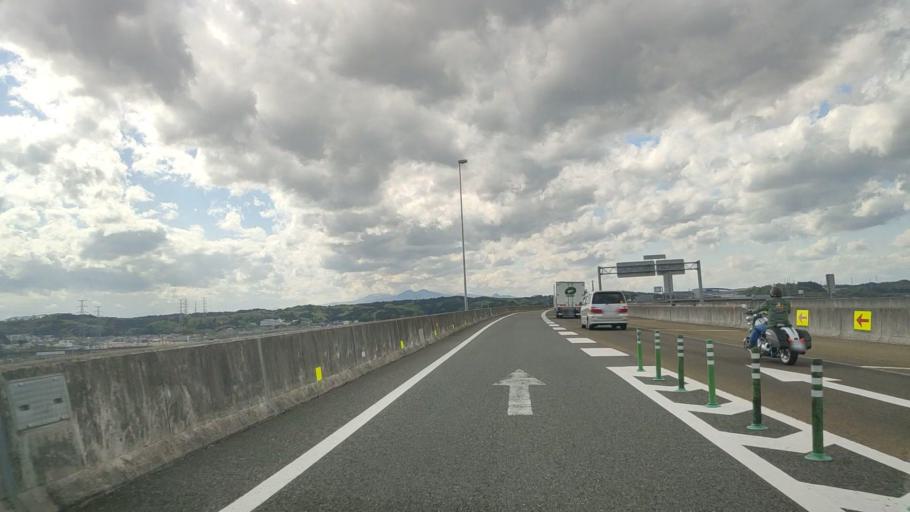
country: JP
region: Miyagi
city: Rifu
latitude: 38.3139
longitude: 140.9731
